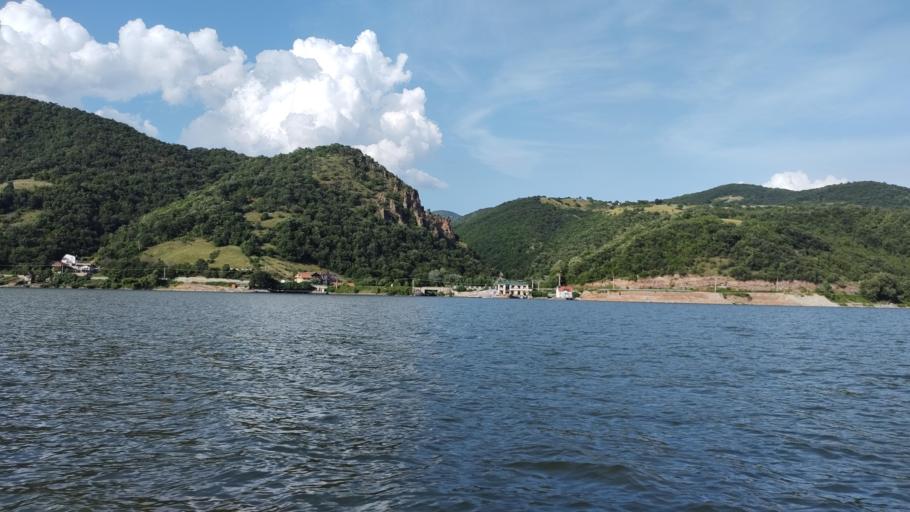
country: RO
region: Mehedinti
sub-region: Comuna Svinita
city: Svinita
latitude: 44.5368
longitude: 22.0595
